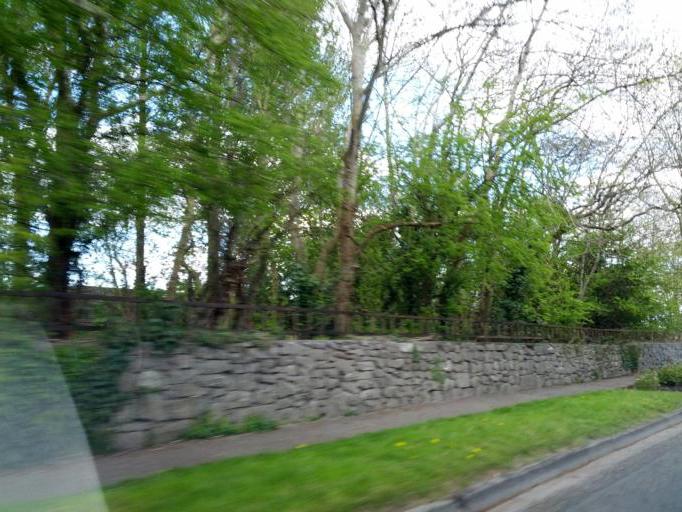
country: IE
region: Connaught
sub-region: County Galway
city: Ballinasloe
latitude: 53.3289
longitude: -8.1913
